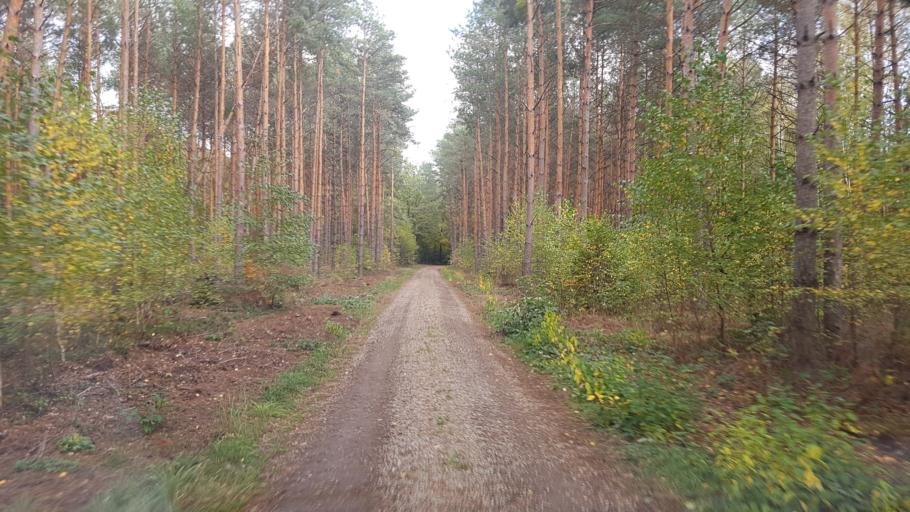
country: DE
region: Brandenburg
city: Schonborn
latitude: 51.6226
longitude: 13.5205
